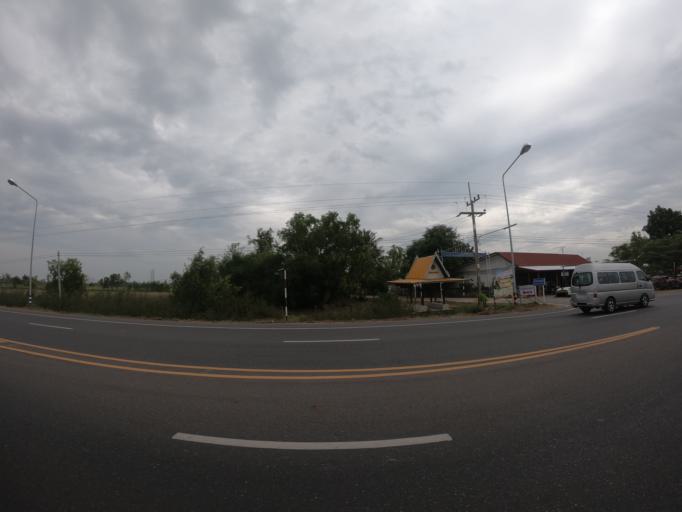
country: TH
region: Roi Et
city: Thawat Buri
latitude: 16.0873
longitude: 103.7581
